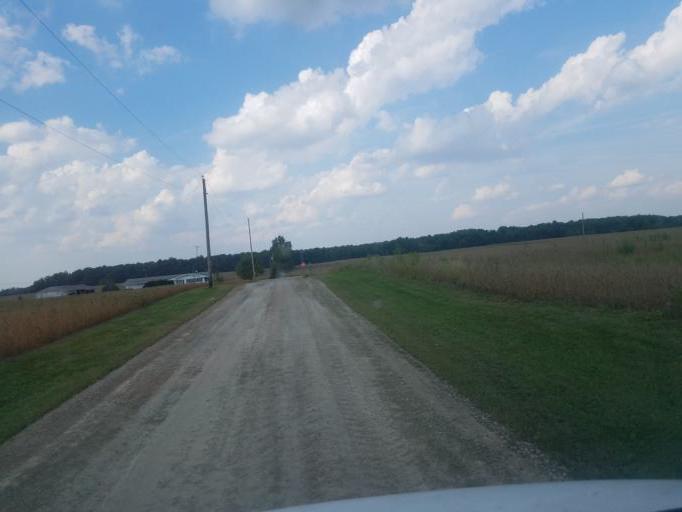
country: US
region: Ohio
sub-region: Hancock County
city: Arlington
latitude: 40.8117
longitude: -83.6897
